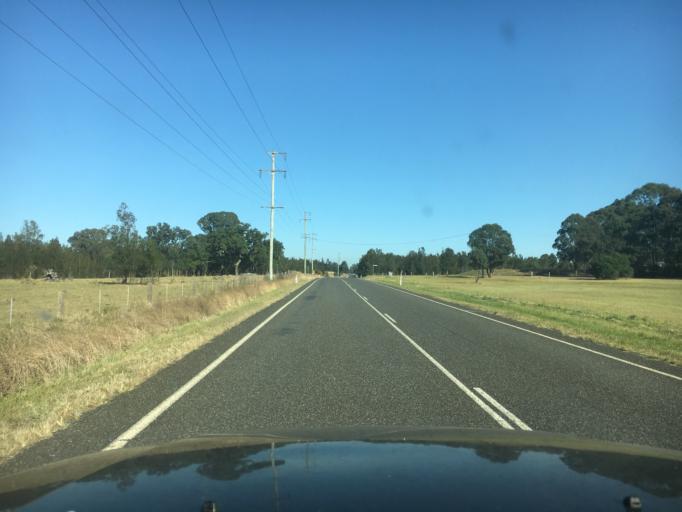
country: AU
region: New South Wales
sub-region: Singleton
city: Singleton
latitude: -32.5462
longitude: 151.2607
